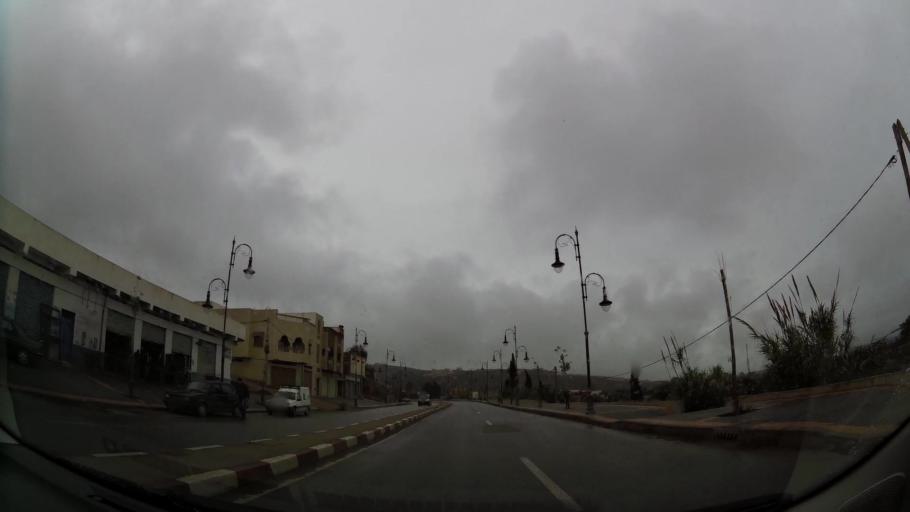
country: MA
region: Taza-Al Hoceima-Taounate
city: Imzourene
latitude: 35.1758
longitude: -3.8749
